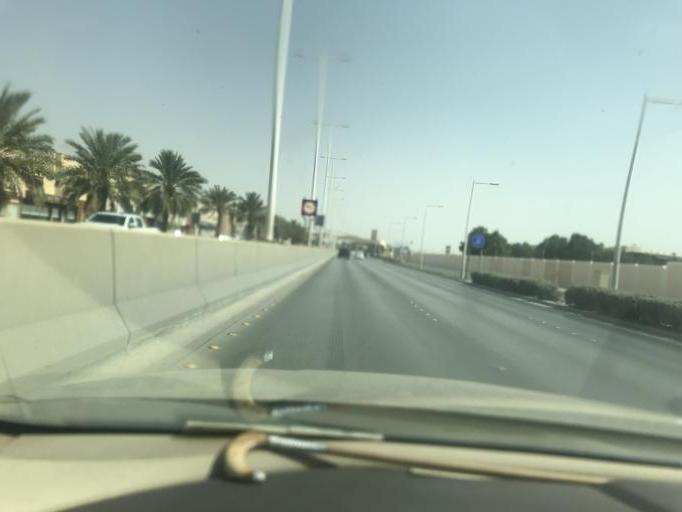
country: SA
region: Ar Riyad
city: Riyadh
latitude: 24.7357
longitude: 46.7076
